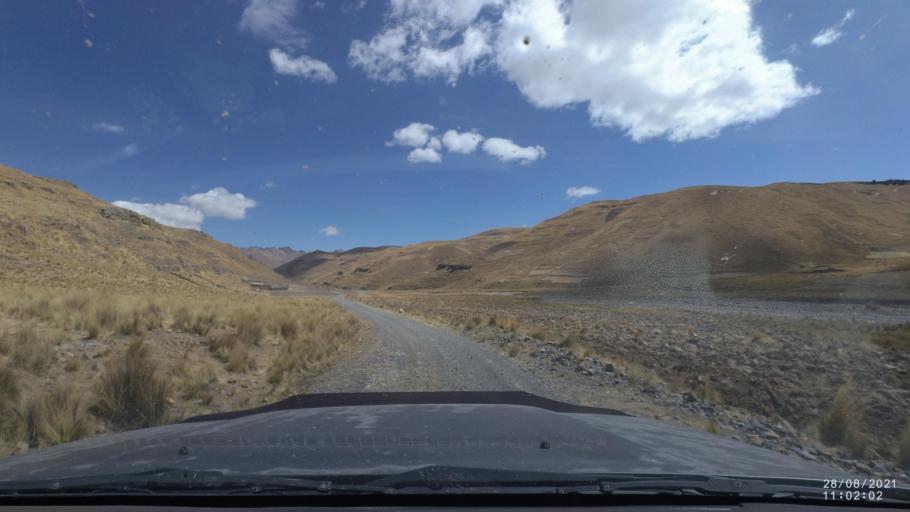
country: BO
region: Cochabamba
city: Cochabamba
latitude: -17.1791
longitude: -66.2697
